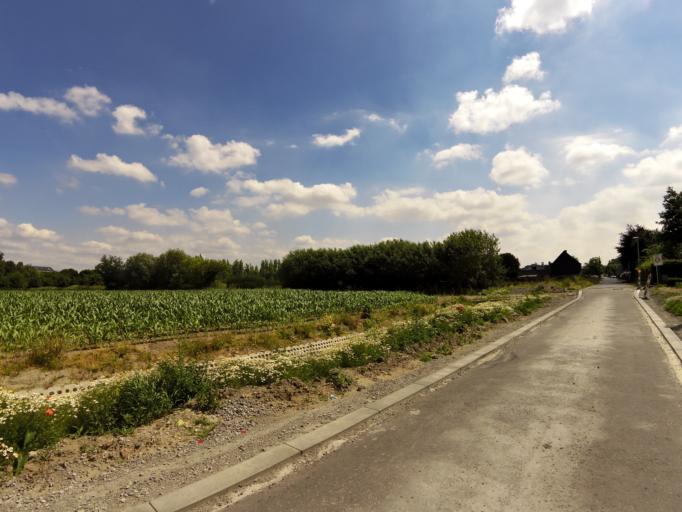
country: BE
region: Flanders
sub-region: Provincie West-Vlaanderen
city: Gistel
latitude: 51.1360
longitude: 2.9839
